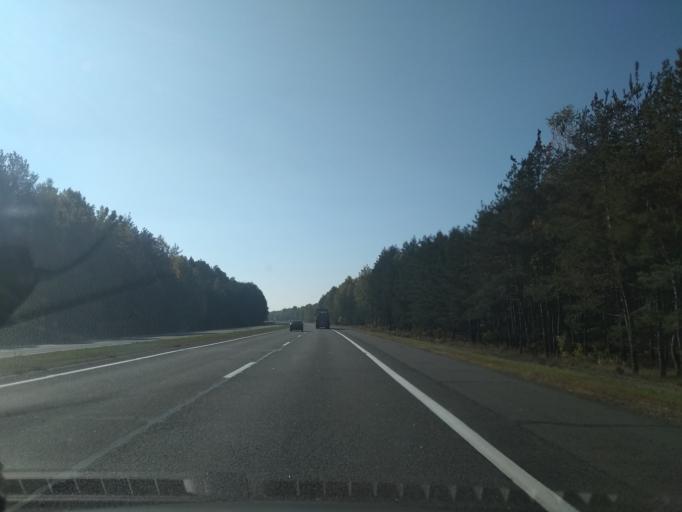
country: BY
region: Brest
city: Ivatsevichy
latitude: 52.8282
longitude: 25.5962
